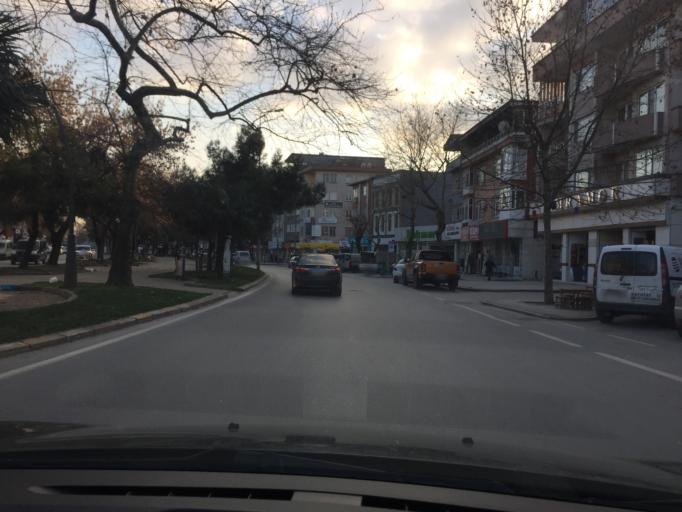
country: TR
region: Sakarya
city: Adapazari
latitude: 40.7847
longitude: 30.3995
